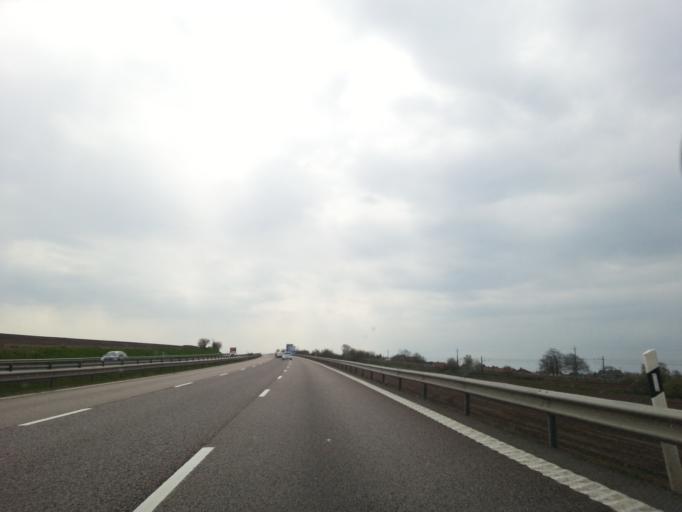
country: SE
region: Skane
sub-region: Helsingborg
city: Glumslov
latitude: 55.9529
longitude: 12.8052
